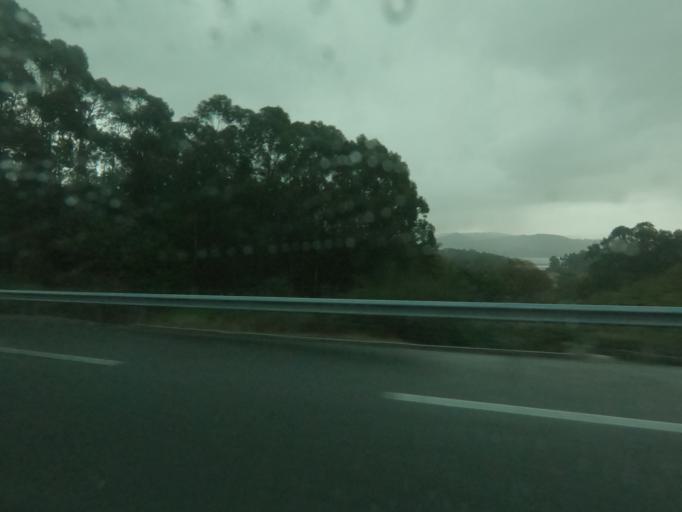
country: ES
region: Galicia
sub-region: Provincia de Pontevedra
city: Marin
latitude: 42.3531
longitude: -8.6448
